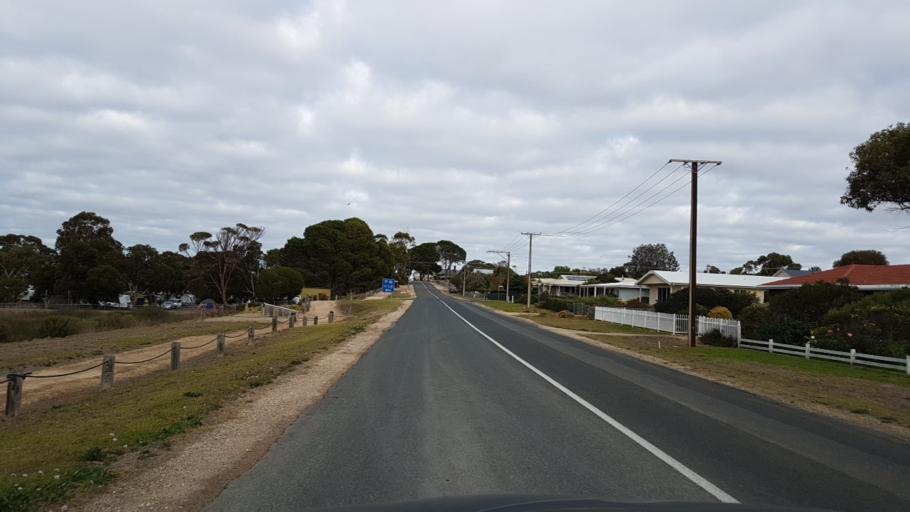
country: AU
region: South Australia
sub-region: Alexandrina
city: Langhorne Creek
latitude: -35.4046
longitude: 138.9770
